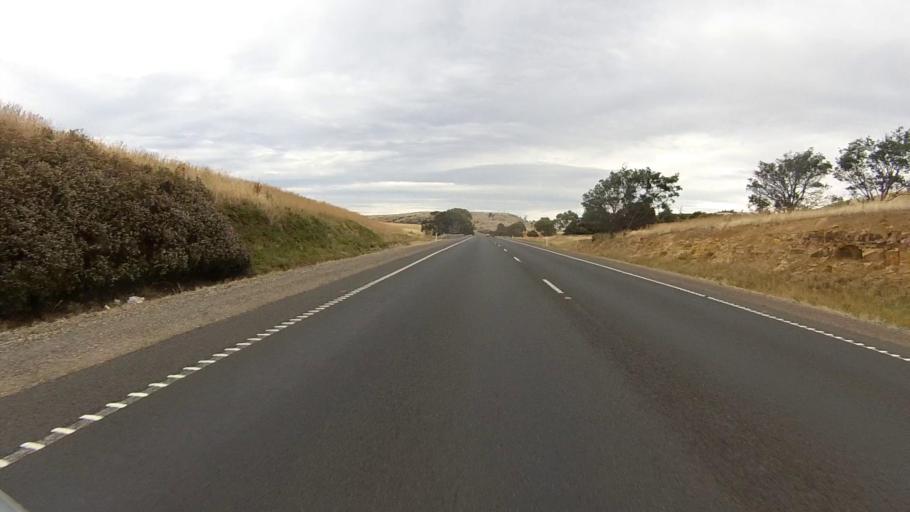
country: AU
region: Tasmania
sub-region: Brighton
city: Bridgewater
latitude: -42.3519
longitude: 147.3372
